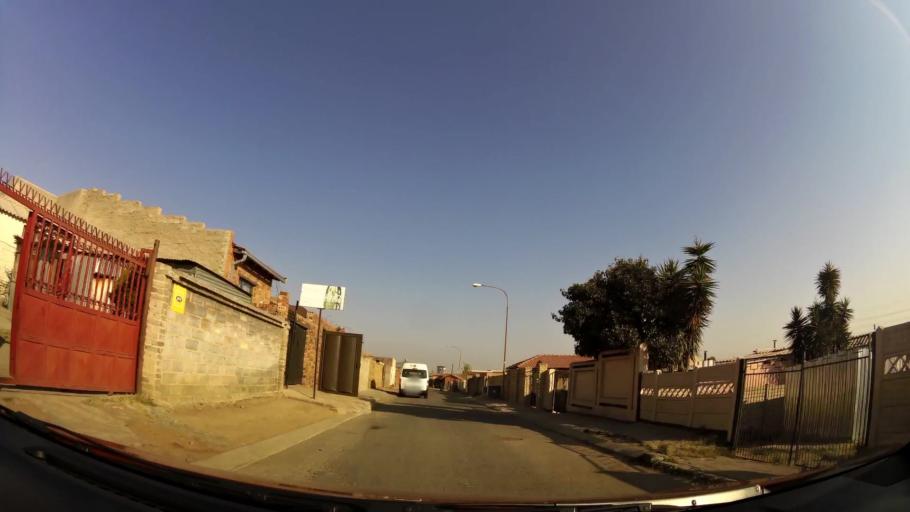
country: ZA
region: Gauteng
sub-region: City of Johannesburg Metropolitan Municipality
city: Soweto
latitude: -26.2571
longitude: 27.9498
